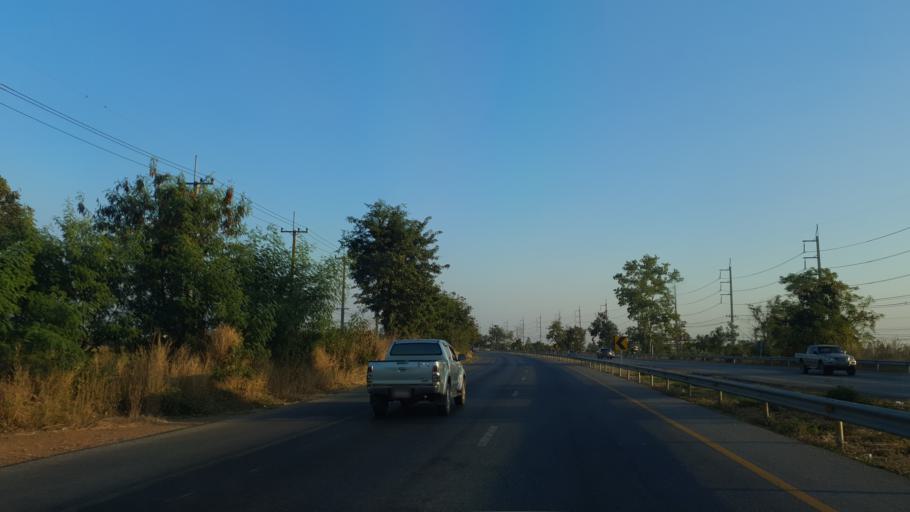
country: TH
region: Kamphaeng Phet
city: Khanu Woralaksaburi
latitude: 16.0662
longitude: 99.7350
